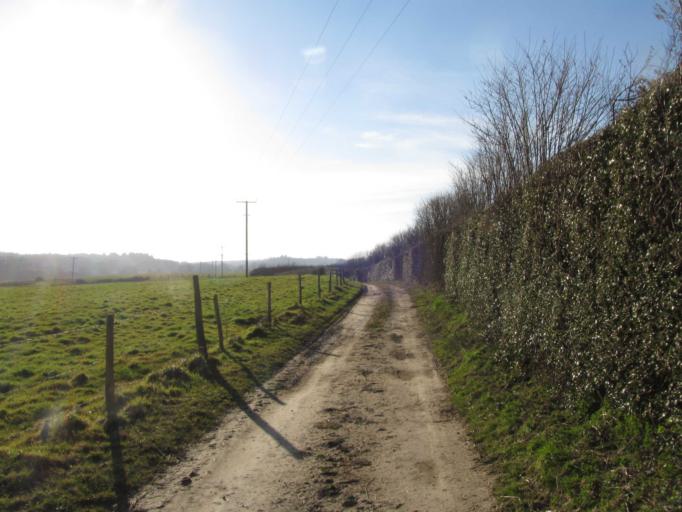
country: GB
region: England
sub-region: West Sussex
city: Petworth
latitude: 50.9735
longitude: -0.6285
